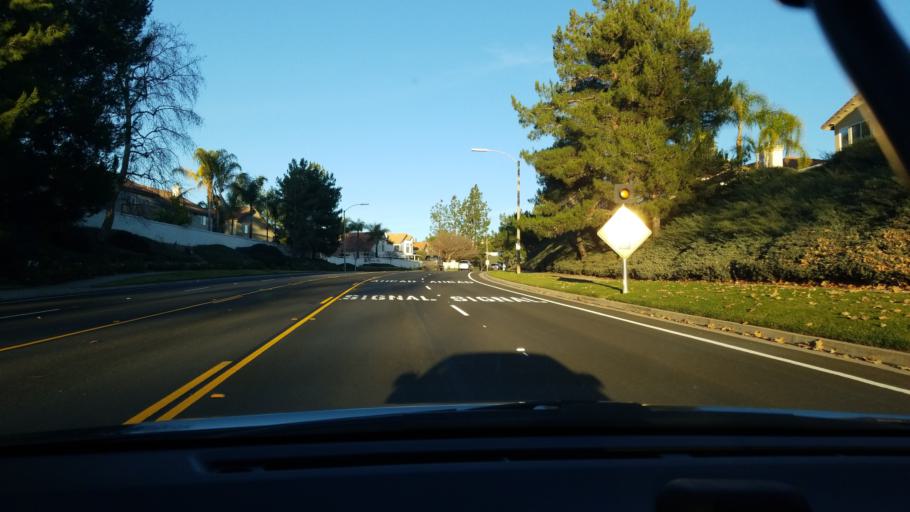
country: US
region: California
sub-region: Riverside County
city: Temecula
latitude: 33.4672
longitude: -117.0981
